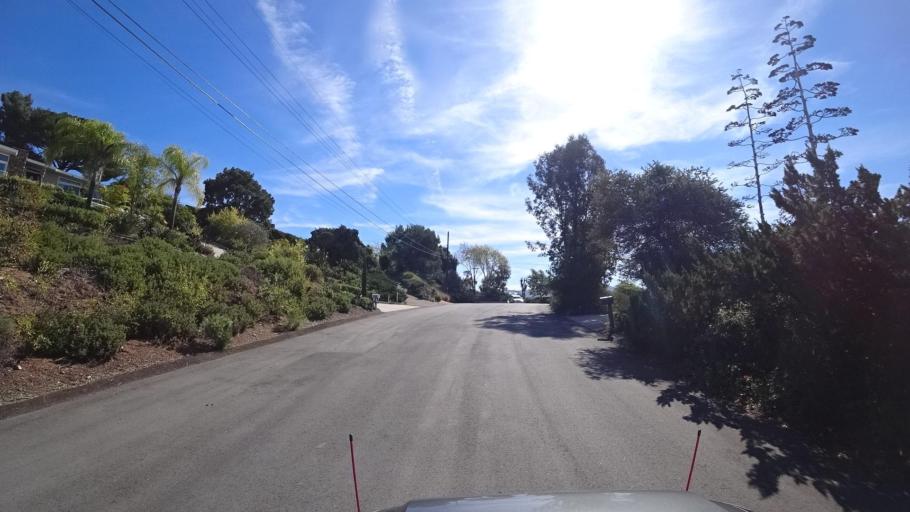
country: US
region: California
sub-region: San Diego County
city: Casa de Oro-Mount Helix
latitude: 32.7566
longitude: -116.9597
